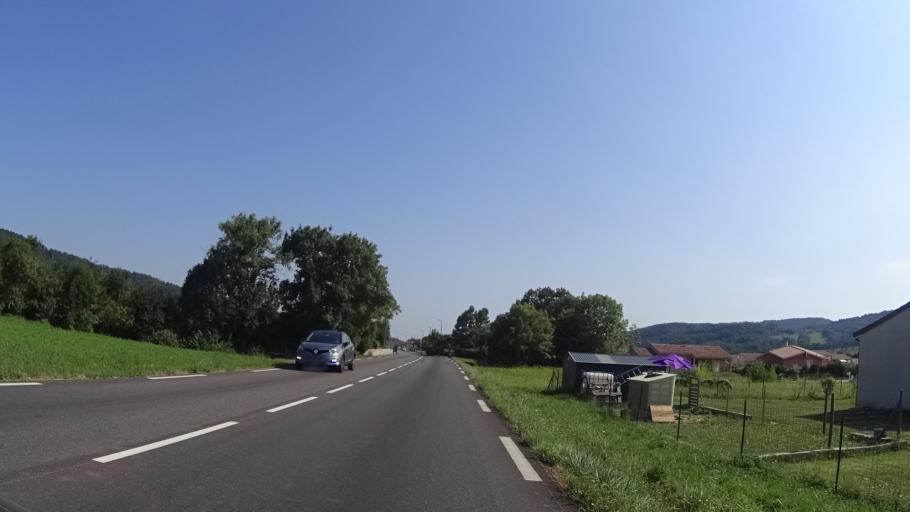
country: FR
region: Midi-Pyrenees
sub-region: Departement de l'Ariege
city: Lavelanet
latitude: 42.9929
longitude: 1.8774
